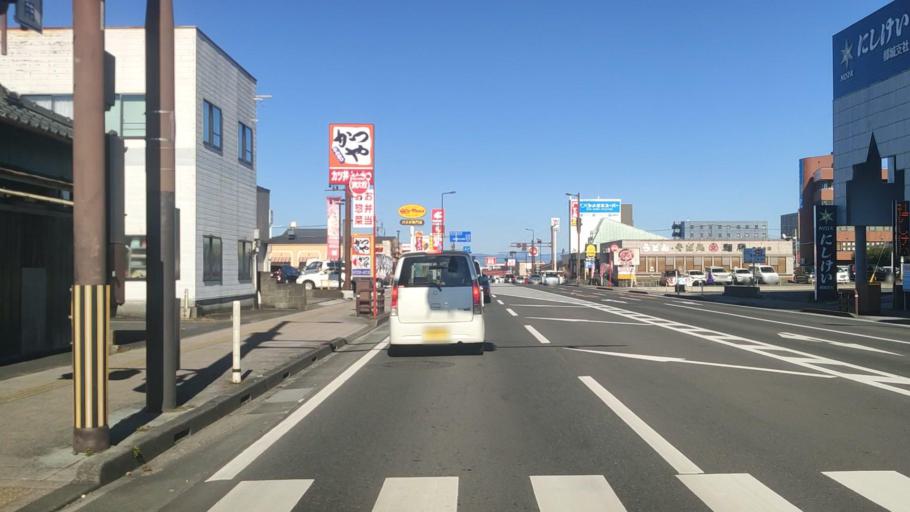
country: JP
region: Miyazaki
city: Miyakonojo
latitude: 31.7338
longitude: 131.0686
